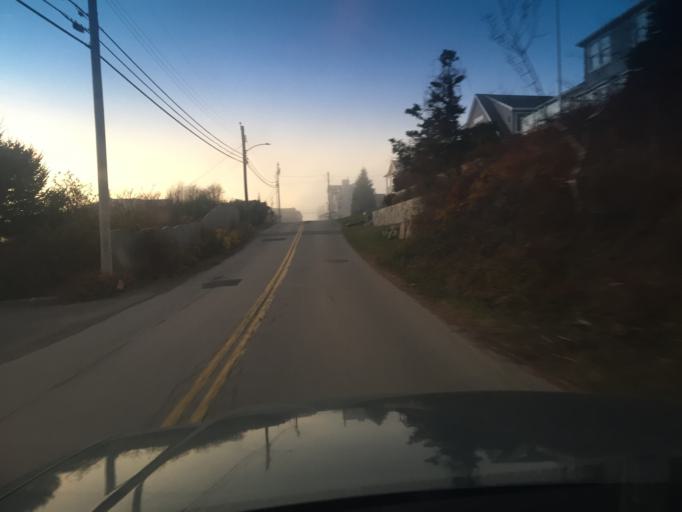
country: US
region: Maine
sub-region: York County
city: York Beach
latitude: 43.1660
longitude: -70.6006
